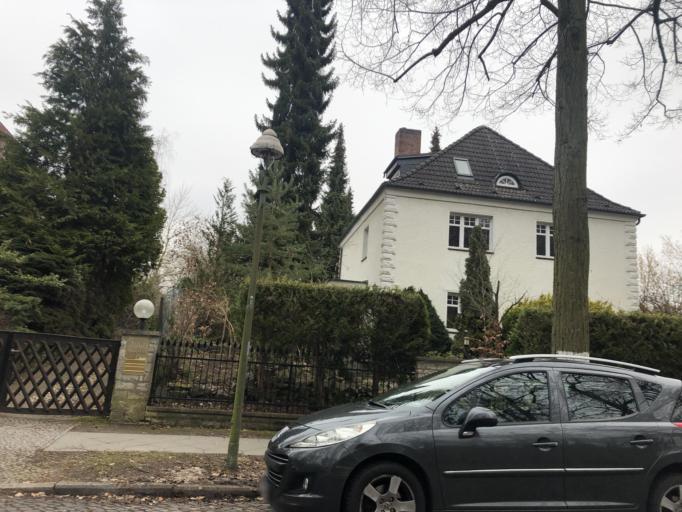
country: DE
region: Berlin
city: Frohnau
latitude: 52.6456
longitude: 13.3021
